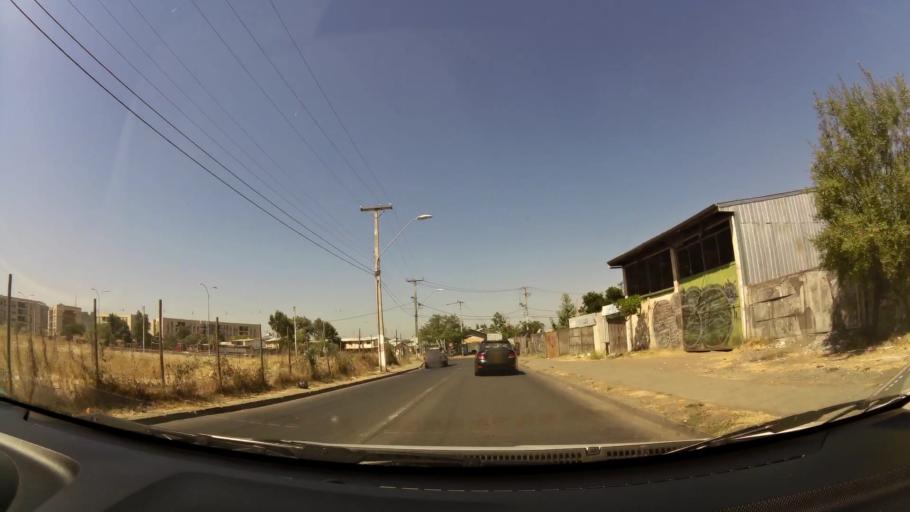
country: CL
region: Maule
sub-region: Provincia de Curico
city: Curico
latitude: -34.9692
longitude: -71.2417
